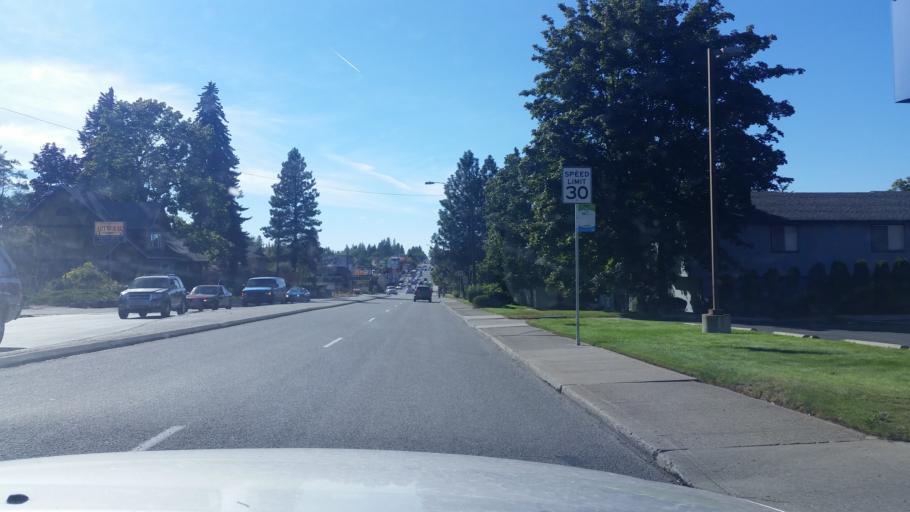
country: US
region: Washington
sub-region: Spokane County
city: Spokane
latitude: 47.6282
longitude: -117.3637
